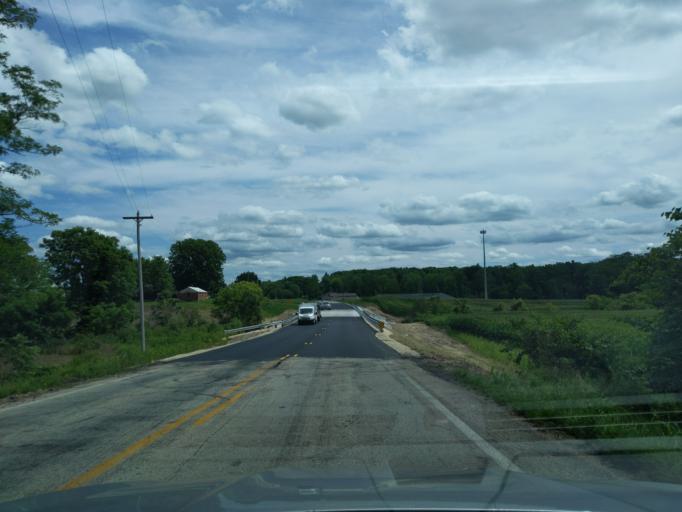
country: US
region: Indiana
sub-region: Ripley County
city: Batesville
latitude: 39.3084
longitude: -85.2406
